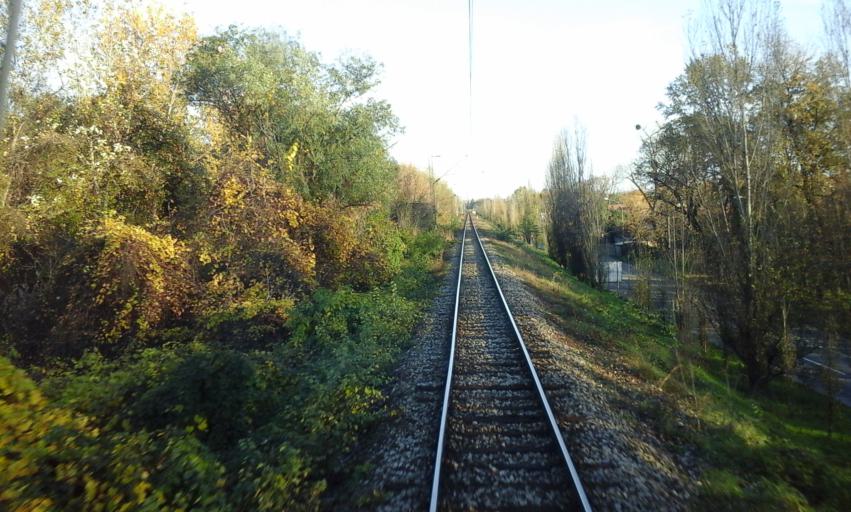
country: RS
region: Autonomna Pokrajina Vojvodina
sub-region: Juznobacki Okrug
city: Petrovaradin
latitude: 45.2586
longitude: 19.8680
